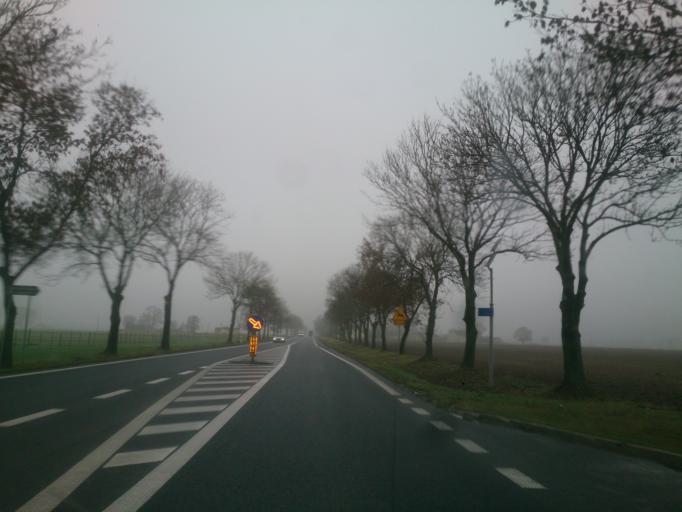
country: PL
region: Masovian Voivodeship
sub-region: Powiat plocki
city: Drobin
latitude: 52.7666
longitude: 19.9379
